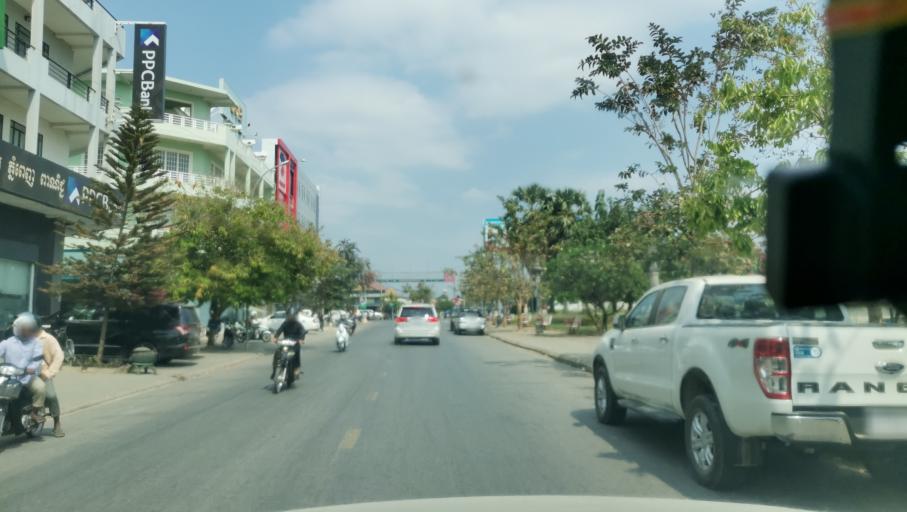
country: KH
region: Battambang
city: Battambang
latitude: 13.1052
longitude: 103.2003
